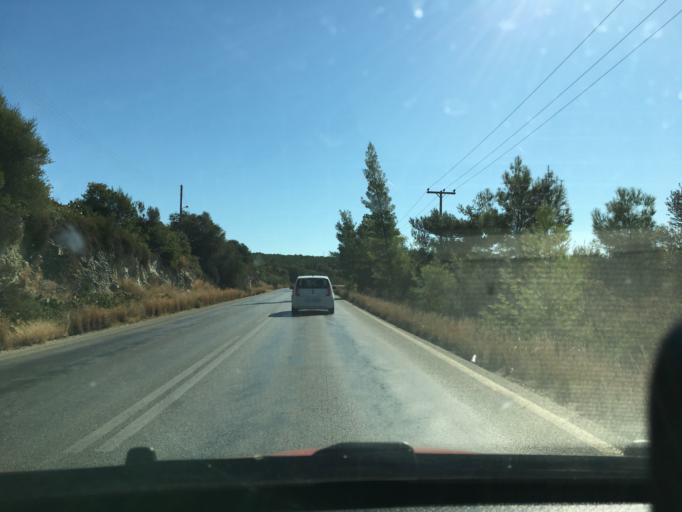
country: GR
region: Central Macedonia
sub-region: Nomos Chalkidikis
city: Kalyves Polygyrou
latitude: 40.2681
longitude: 23.4572
